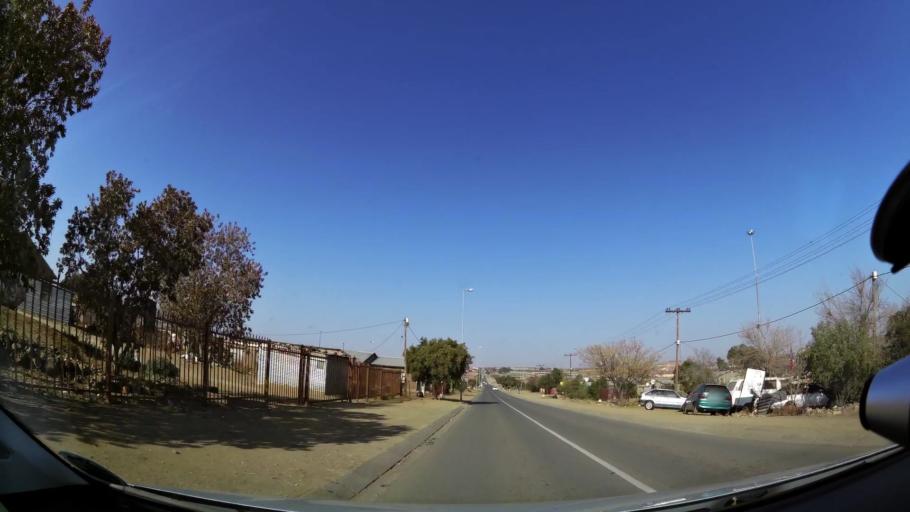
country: ZA
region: Orange Free State
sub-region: Mangaung Metropolitan Municipality
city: Bloemfontein
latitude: -29.1780
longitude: 26.2249
